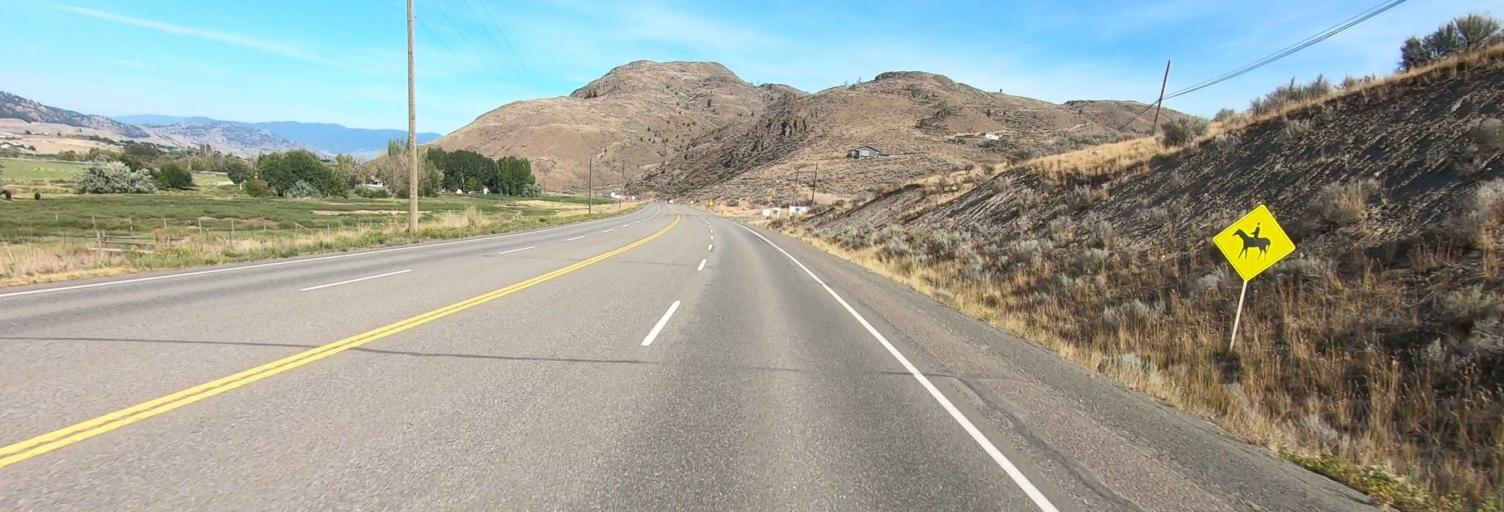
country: CA
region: British Columbia
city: Kamloops
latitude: 50.6988
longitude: -120.5905
